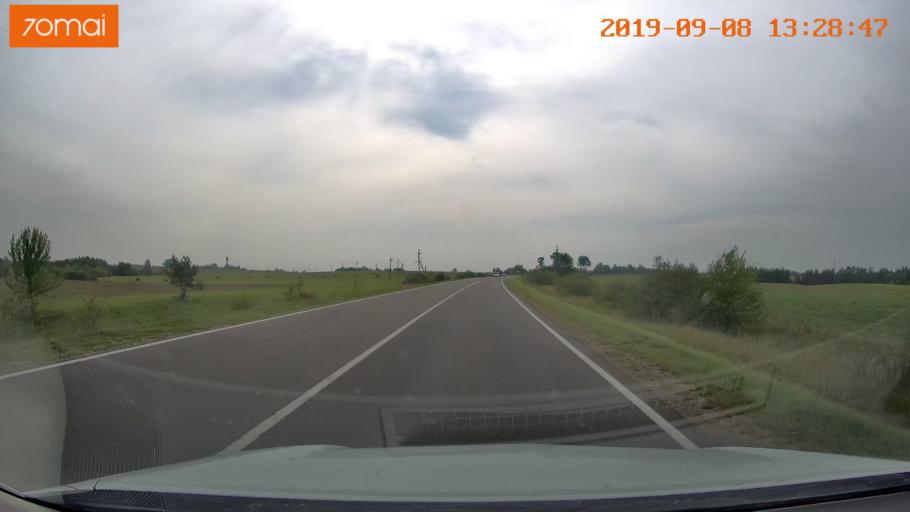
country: LT
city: Jieznas
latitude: 54.5715
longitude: 24.1680
